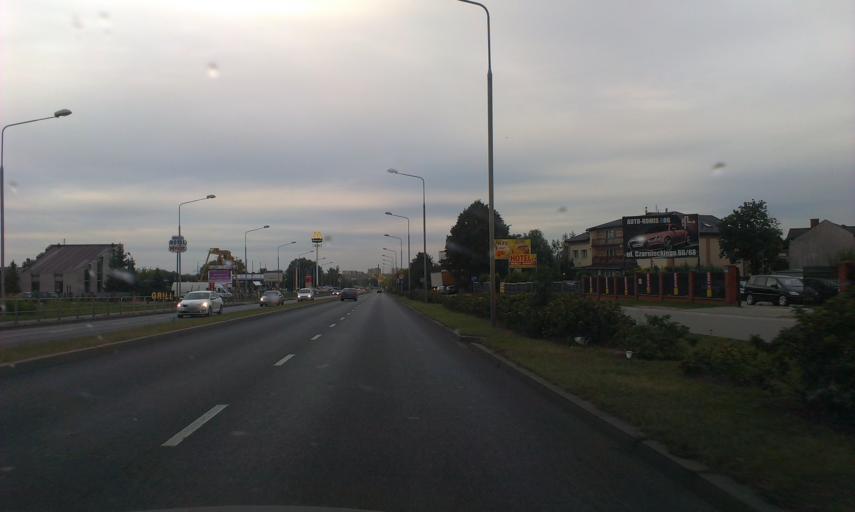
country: PL
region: Masovian Voivodeship
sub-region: Radom
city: Radom
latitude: 51.4154
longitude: 21.1339
